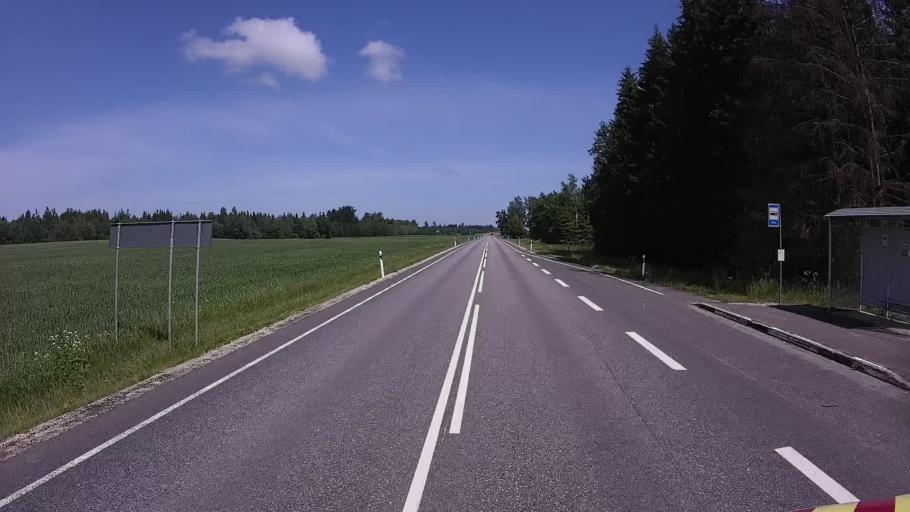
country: EE
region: Tartu
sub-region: Tartu linn
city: Tartu
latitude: 58.3785
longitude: 26.8850
